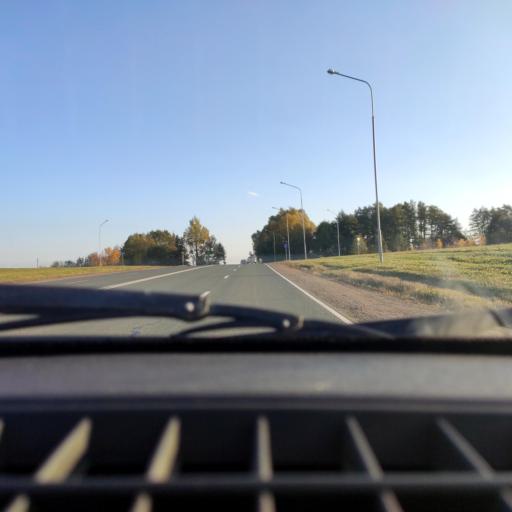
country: RU
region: Bashkortostan
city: Avdon
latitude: 54.6635
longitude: 55.7351
